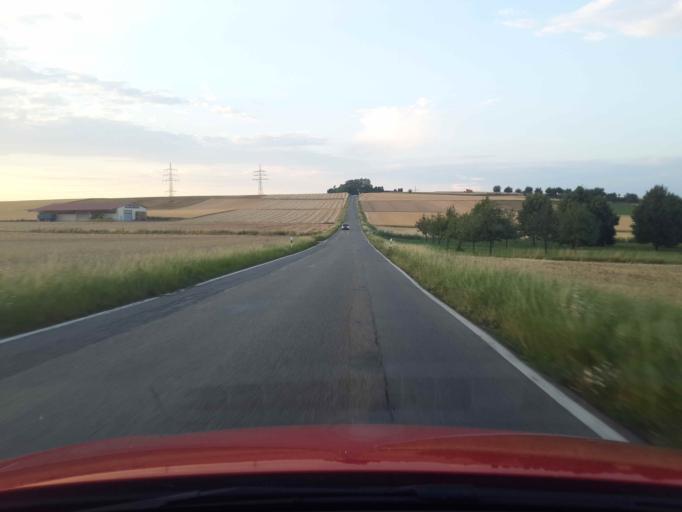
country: DE
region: Baden-Wuerttemberg
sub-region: Regierungsbezirk Stuttgart
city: Nordheim
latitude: 49.1186
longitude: 9.1294
